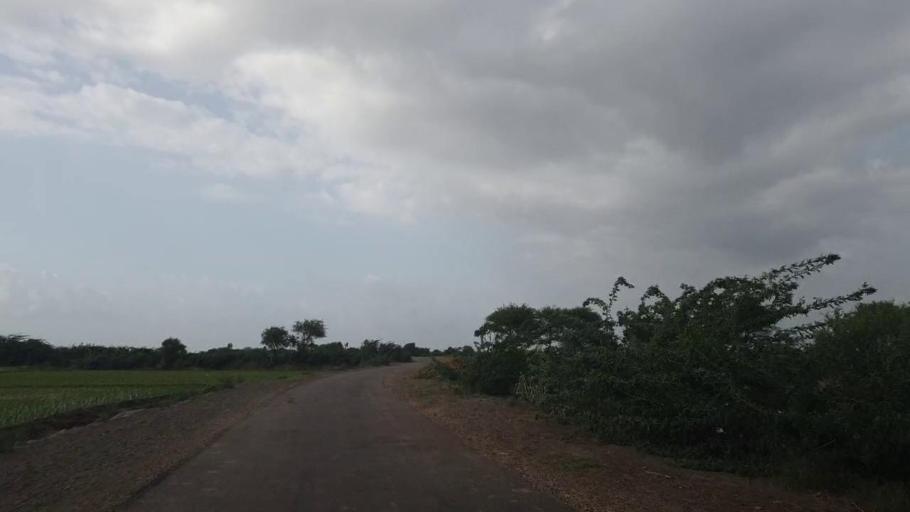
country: PK
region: Sindh
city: Kadhan
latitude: 24.6032
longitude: 69.0554
